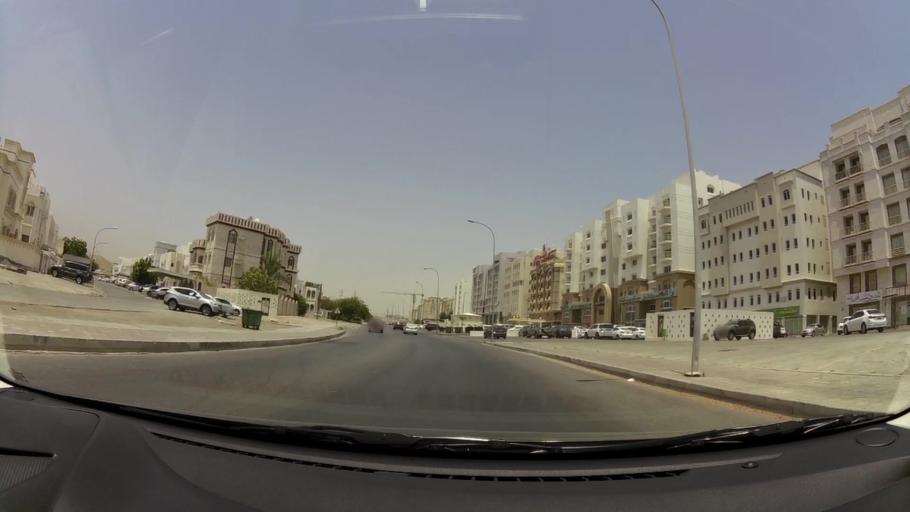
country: OM
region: Muhafazat Masqat
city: Bawshar
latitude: 23.5842
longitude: 58.4285
